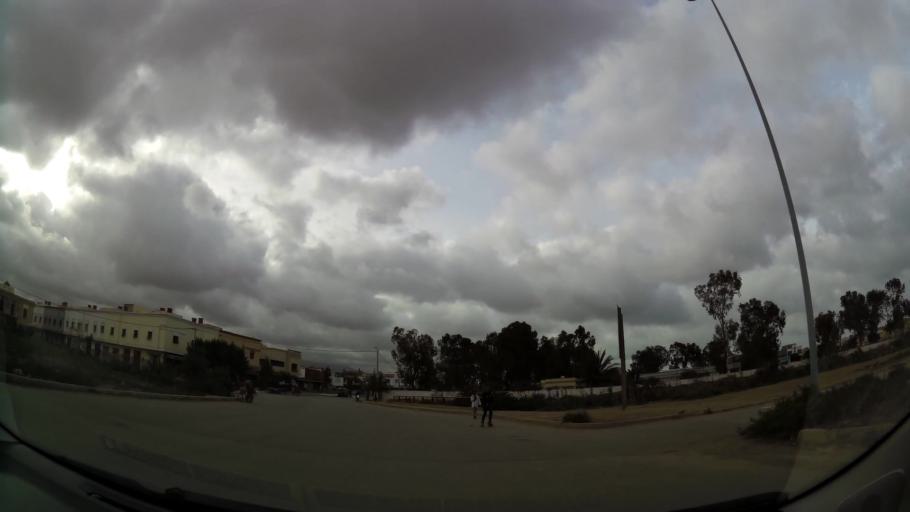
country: MA
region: Oriental
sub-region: Nador
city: Nador
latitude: 35.1602
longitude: -2.9154
